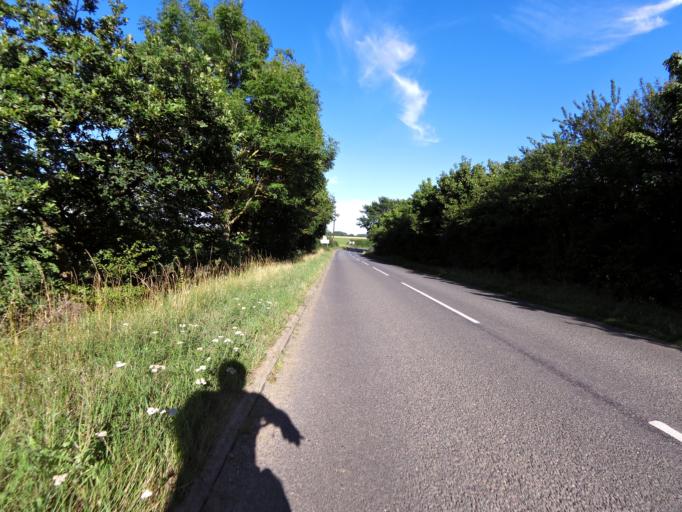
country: GB
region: England
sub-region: Suffolk
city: Kesgrave
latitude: 52.0349
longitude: 1.2597
